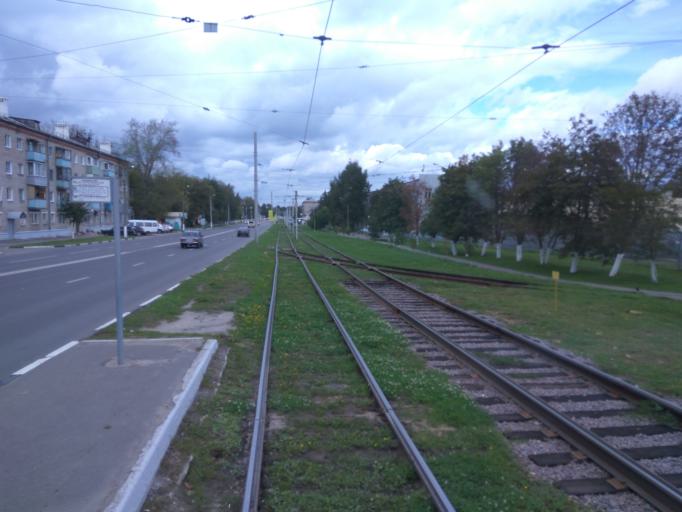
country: RU
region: Moskovskaya
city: Kolomna
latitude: 55.0880
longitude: 38.7658
